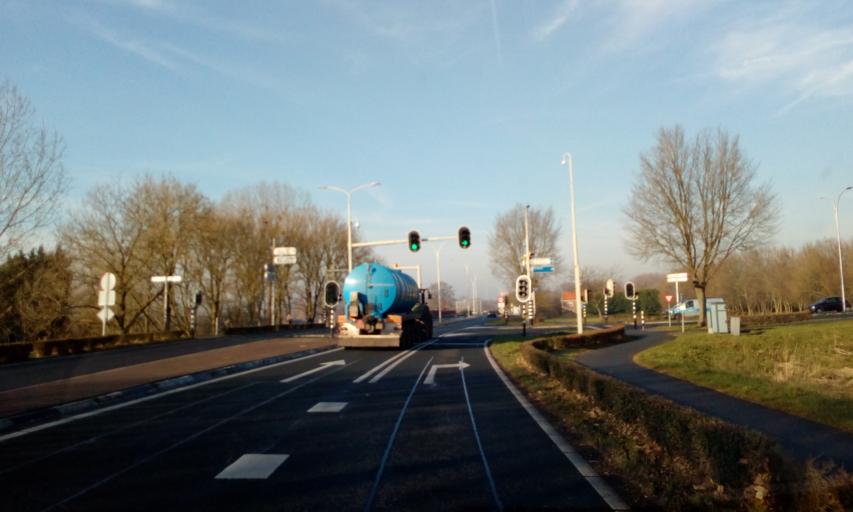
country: NL
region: South Holland
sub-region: Gemeente Vlist
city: Haastrecht
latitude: 52.0035
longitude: 4.7416
